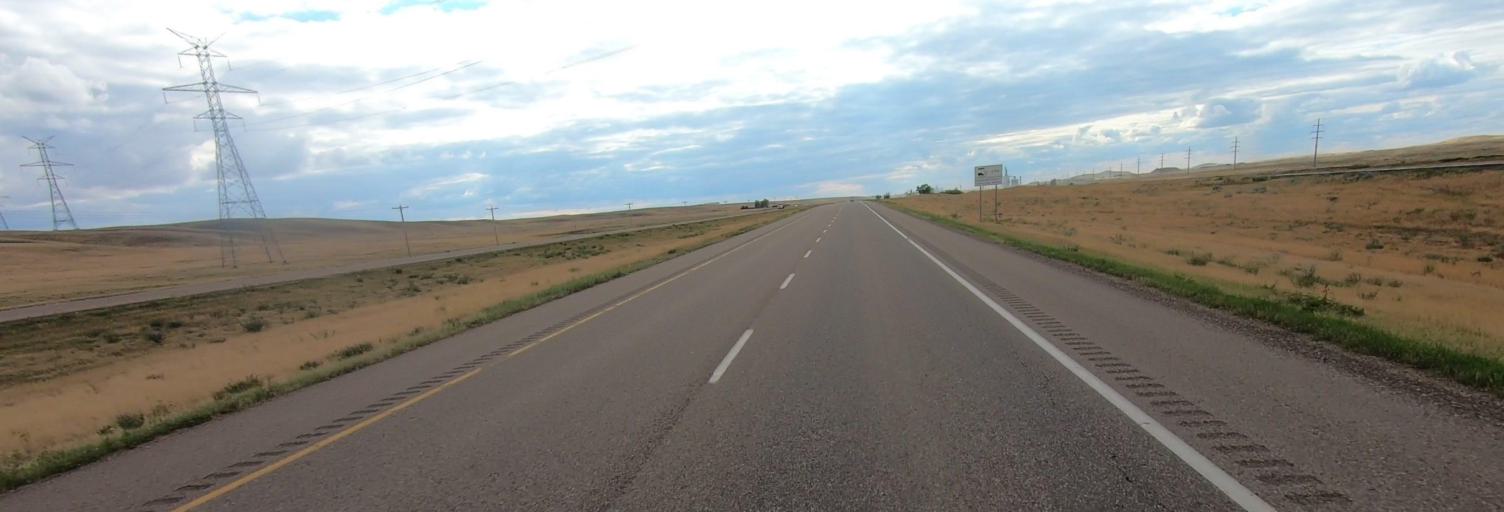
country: CA
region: Alberta
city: Medicine Hat
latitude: 49.9781
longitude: -110.4913
